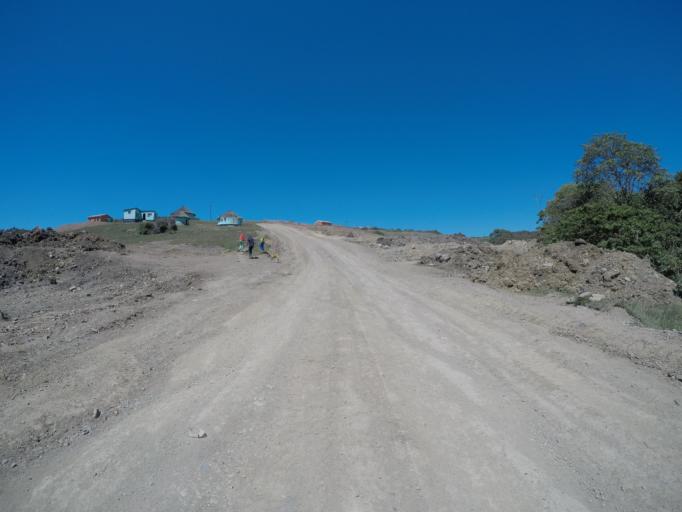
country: ZA
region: Eastern Cape
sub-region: OR Tambo District Municipality
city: Libode
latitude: -32.0187
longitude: 29.1153
